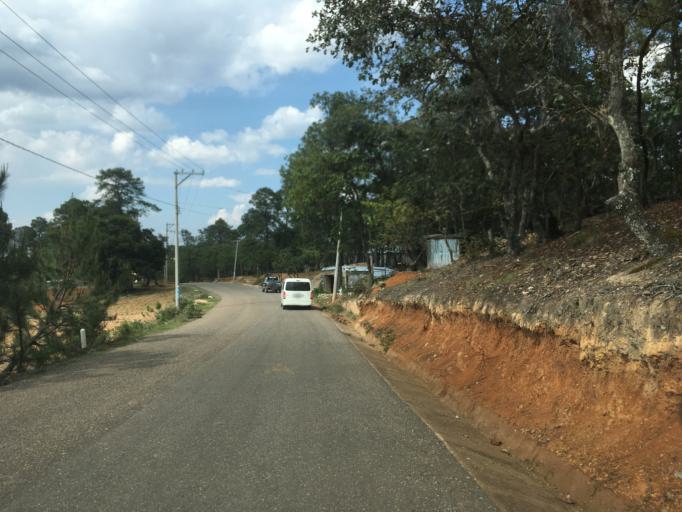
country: MX
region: Oaxaca
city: Santiago Tilantongo
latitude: 17.2151
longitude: -97.2804
